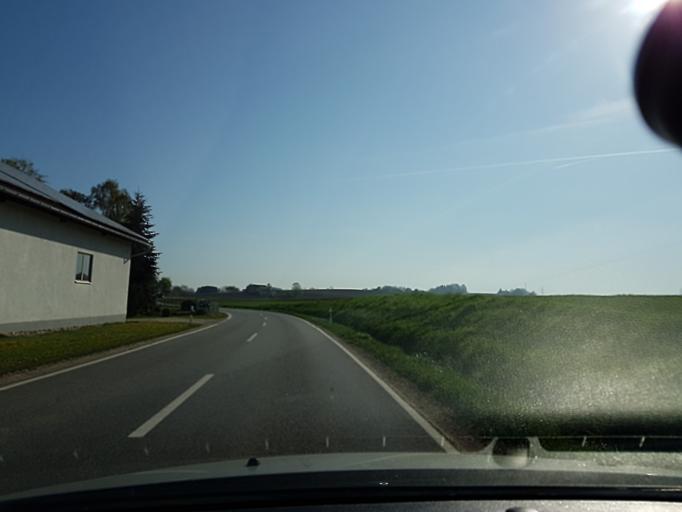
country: DE
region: Bavaria
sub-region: Lower Bavaria
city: Eging
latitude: 48.4507
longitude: 12.1840
